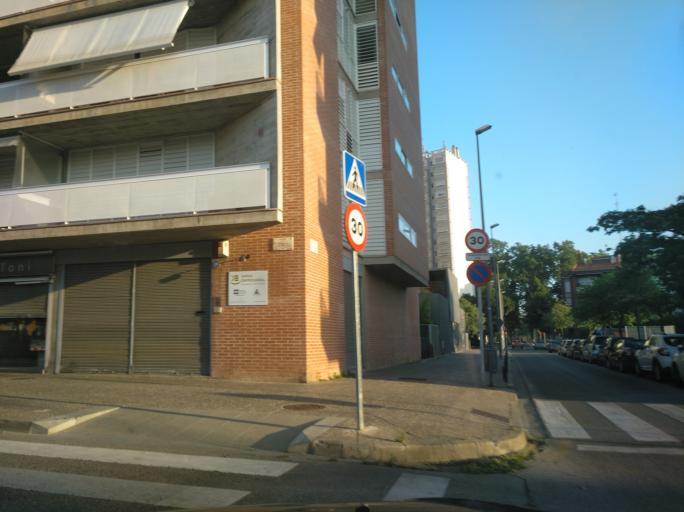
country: ES
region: Catalonia
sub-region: Provincia de Girona
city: Girona
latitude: 41.9834
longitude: 2.8141
